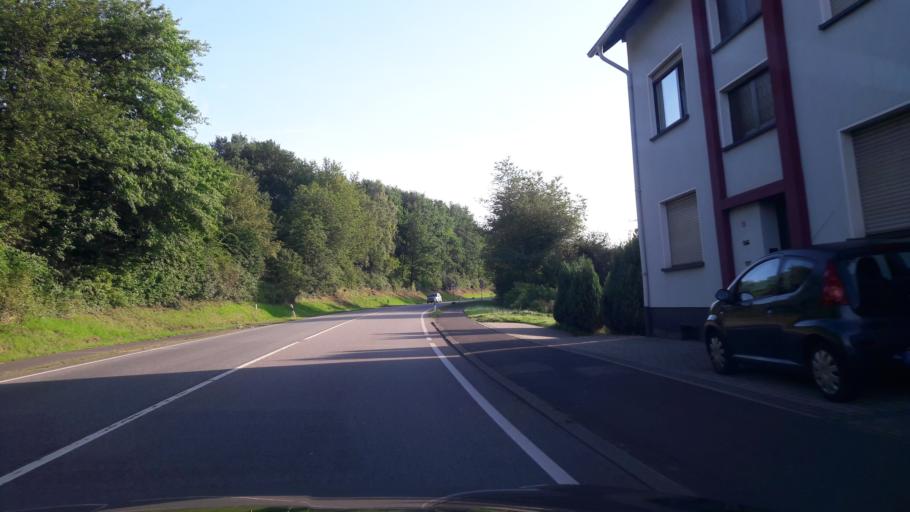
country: DE
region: Saarland
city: Heusweiler
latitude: 49.3527
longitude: 6.9320
